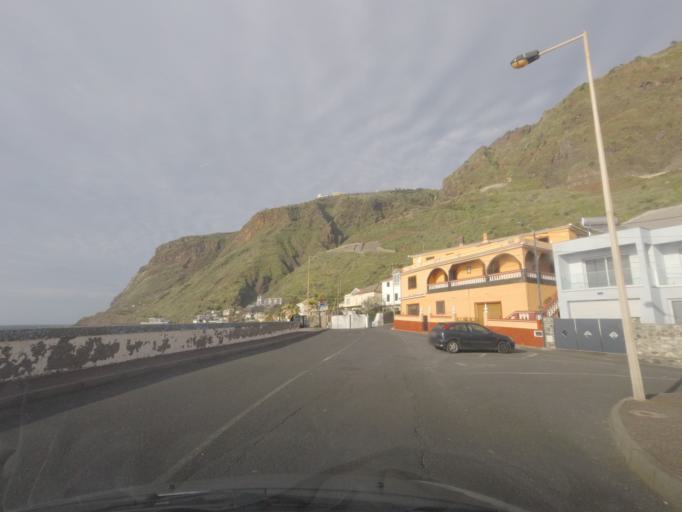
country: PT
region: Madeira
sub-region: Calheta
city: Faja da Ovelha
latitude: 32.7616
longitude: -17.2329
